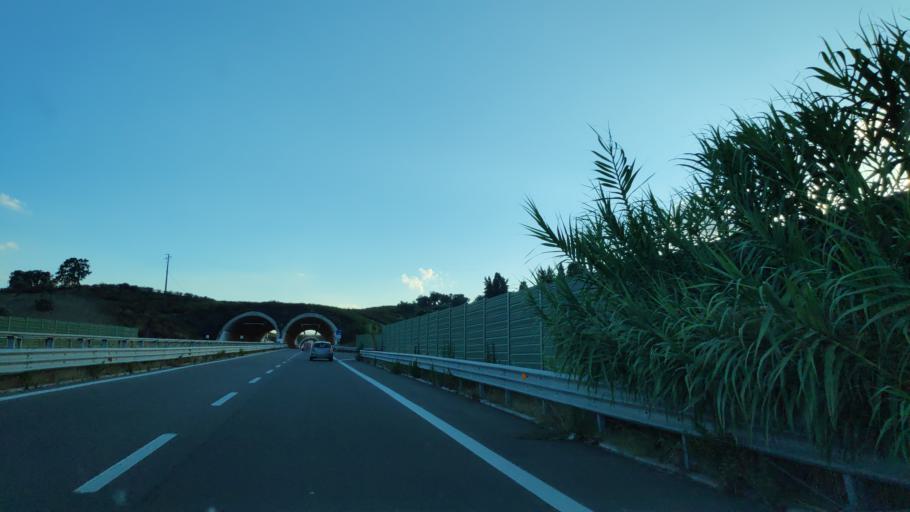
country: IT
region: Calabria
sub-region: Provincia di Reggio Calabria
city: Locri
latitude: 38.2473
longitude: 16.2531
